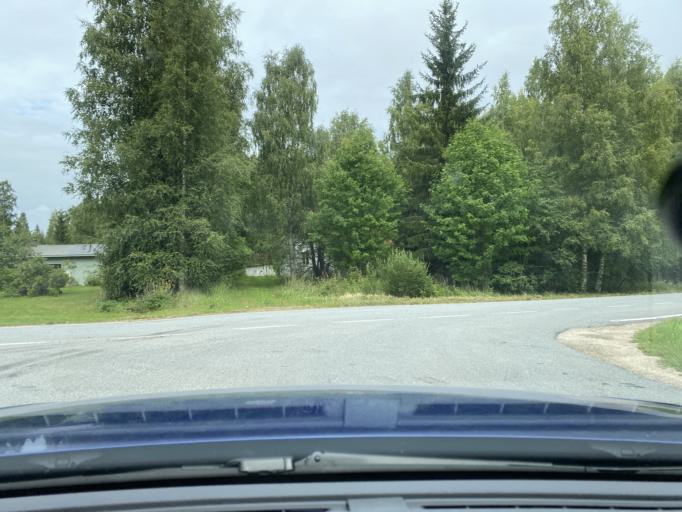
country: FI
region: Pirkanmaa
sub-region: Ylae-Pirkanmaa
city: Maenttae
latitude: 62.0273
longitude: 24.7154
